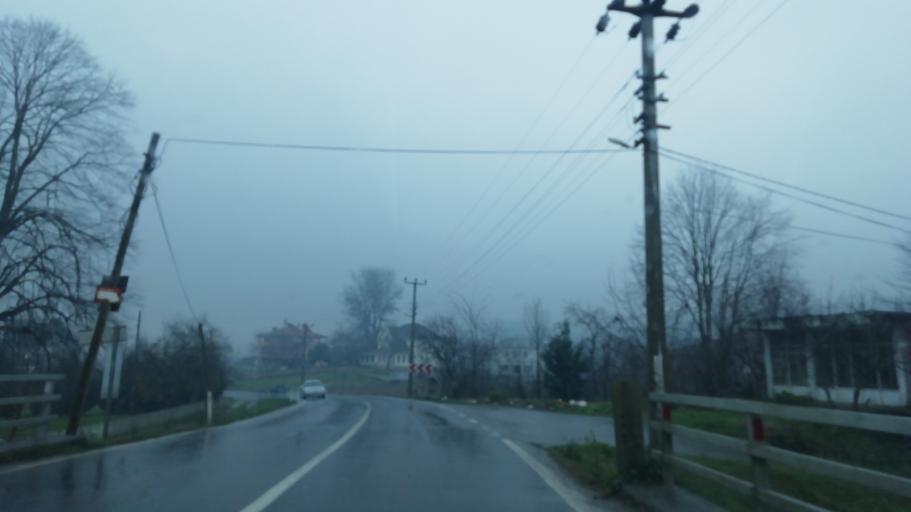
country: TR
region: Sakarya
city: Karapurcek
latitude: 40.6889
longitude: 30.4793
